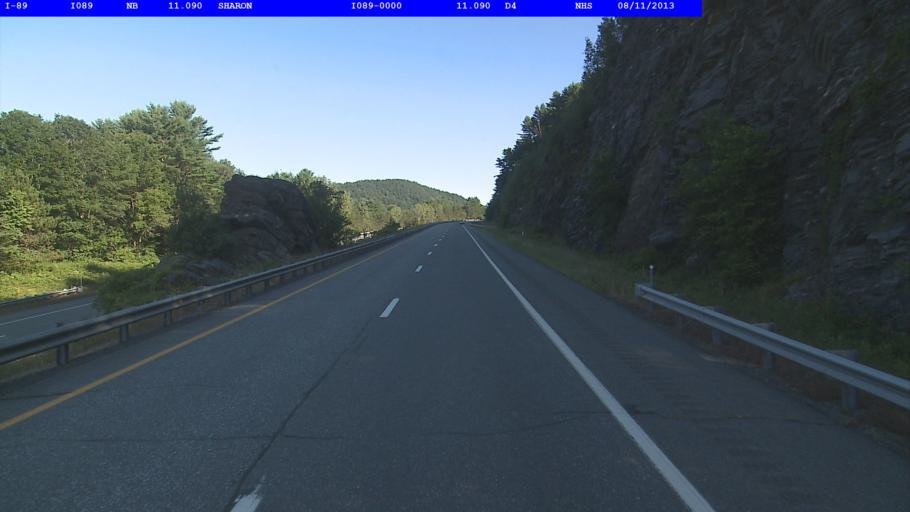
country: US
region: Vermont
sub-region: Windsor County
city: Woodstock
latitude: 43.7551
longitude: -72.4468
